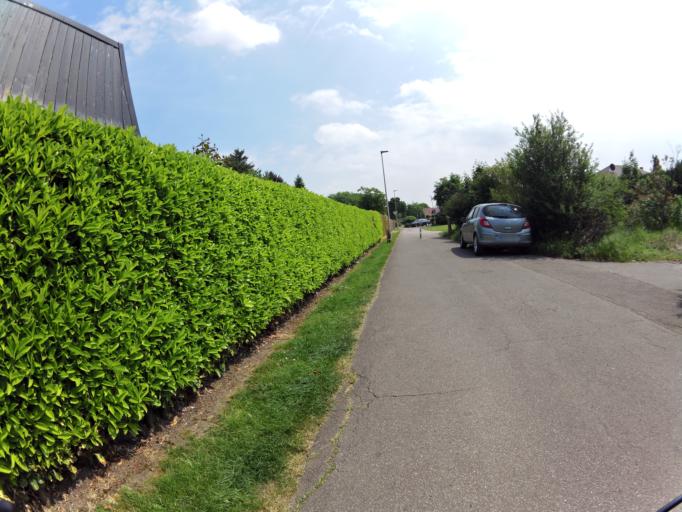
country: DE
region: North Rhine-Westphalia
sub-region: Regierungsbezirk Koln
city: Gangelt
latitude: 51.0051
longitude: 6.0494
